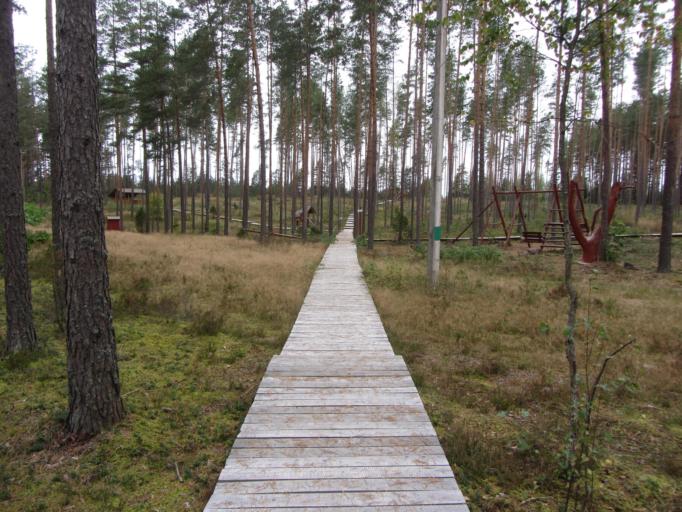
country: LT
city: Svencioneliai
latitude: 55.1903
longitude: 25.9936
